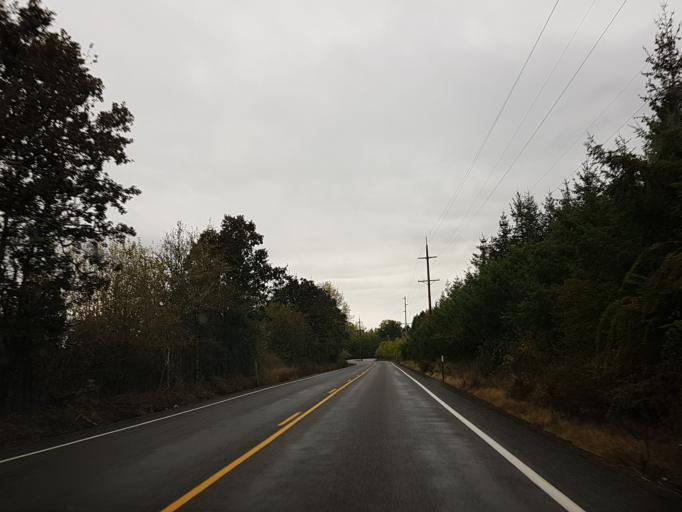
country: US
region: Oregon
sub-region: Marion County
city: Stayton
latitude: 44.7120
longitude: -122.7815
